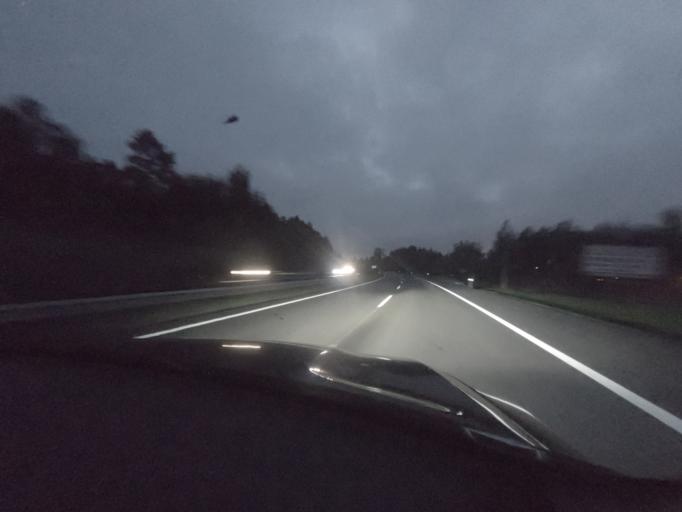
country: PT
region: Leiria
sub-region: Leiria
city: Caranguejeira
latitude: 39.7926
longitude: -8.7351
